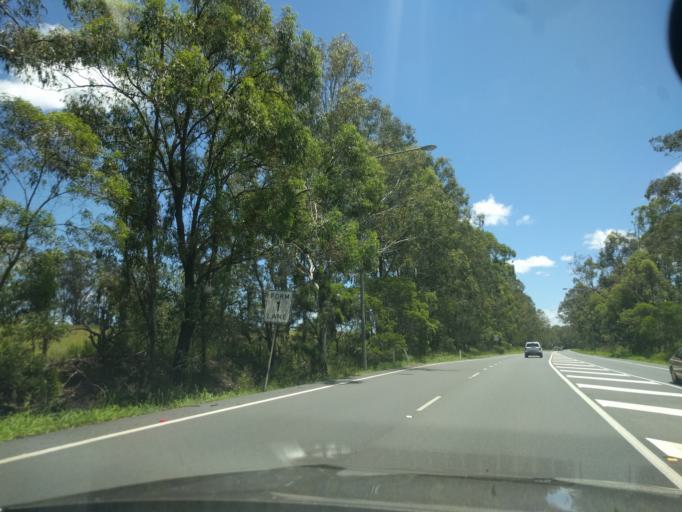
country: AU
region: Queensland
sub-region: Logan
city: Cedar Vale
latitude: -27.8624
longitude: 153.0008
